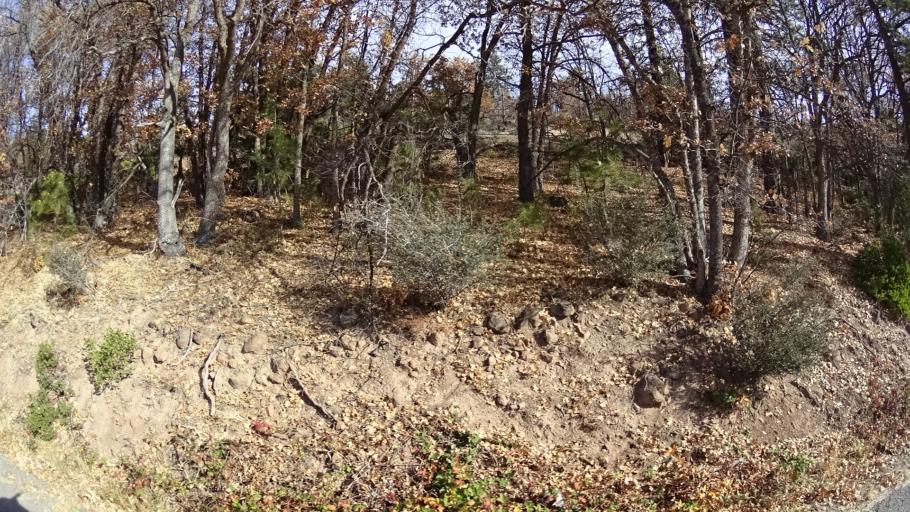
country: US
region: California
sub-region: Siskiyou County
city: Weed
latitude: 41.4452
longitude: -122.4244
